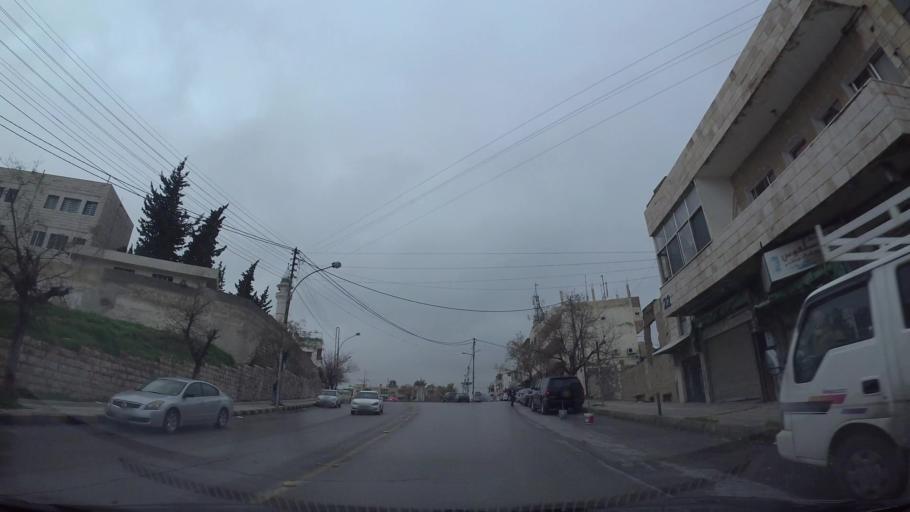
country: JO
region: Amman
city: Amman
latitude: 31.9586
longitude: 35.9321
